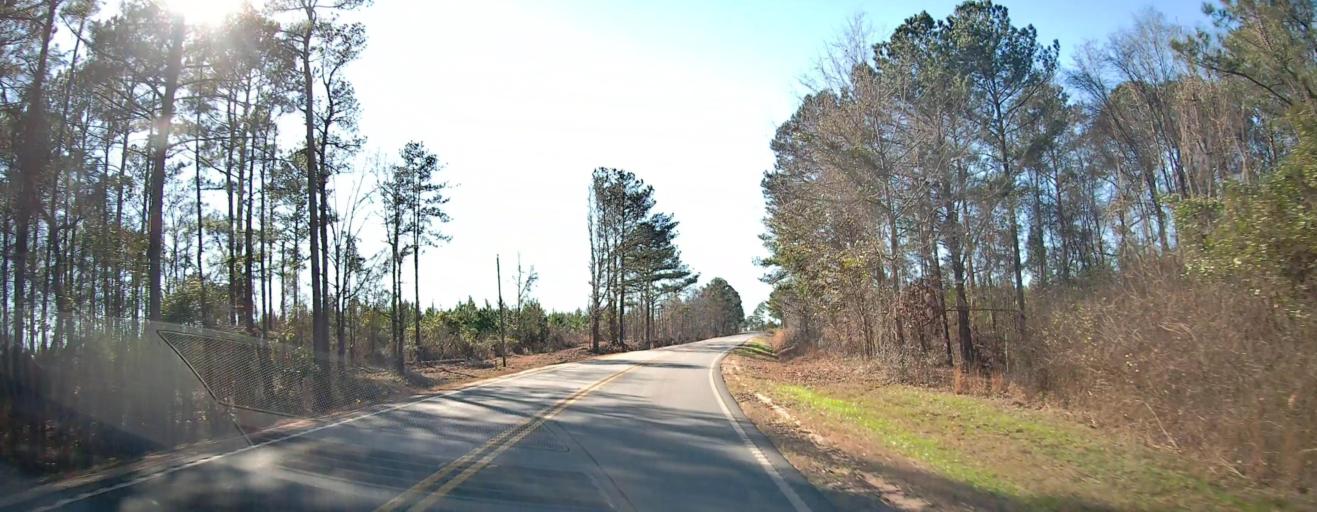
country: US
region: Georgia
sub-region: Taylor County
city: Butler
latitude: 32.6601
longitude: -84.3487
